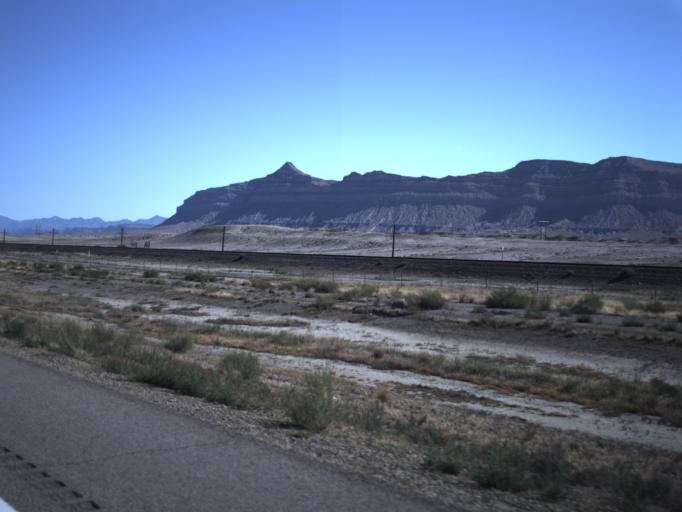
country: US
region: Utah
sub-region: Carbon County
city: East Carbon City
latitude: 39.1185
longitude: -110.3294
